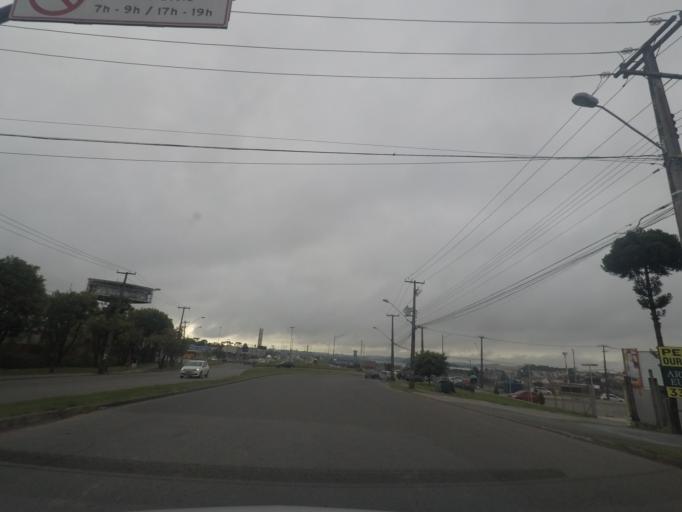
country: BR
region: Parana
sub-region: Pinhais
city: Pinhais
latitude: -25.3886
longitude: -49.2072
